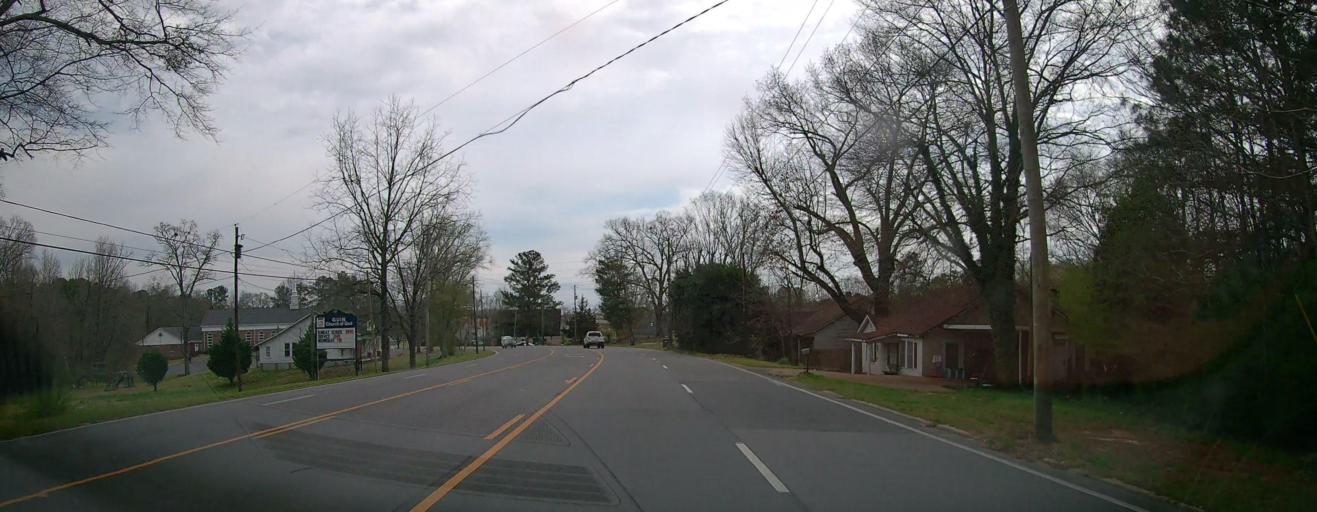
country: US
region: Alabama
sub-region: Marion County
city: Guin
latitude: 33.9794
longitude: -87.9175
